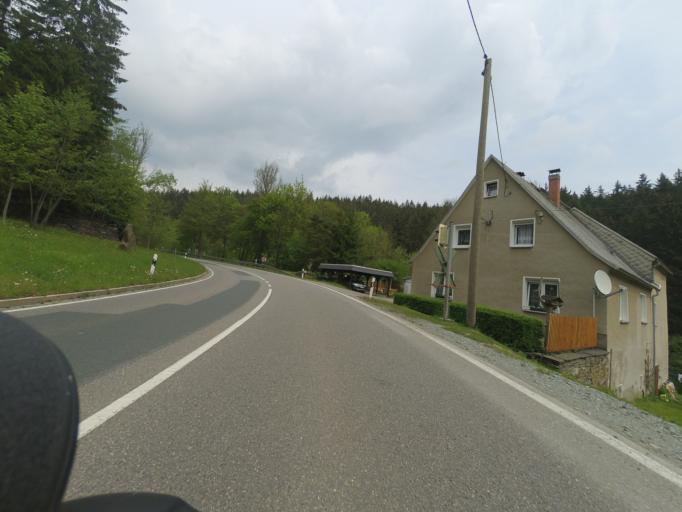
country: DE
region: Saxony
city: Pobershau
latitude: 50.6551
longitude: 13.1978
